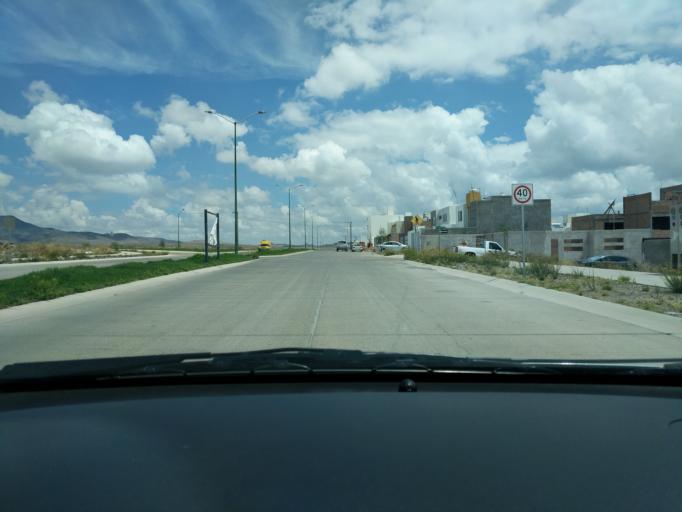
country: MX
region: San Luis Potosi
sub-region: Mexquitic de Carmona
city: Guadalupe Victoria
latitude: 22.1582
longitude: -101.0542
